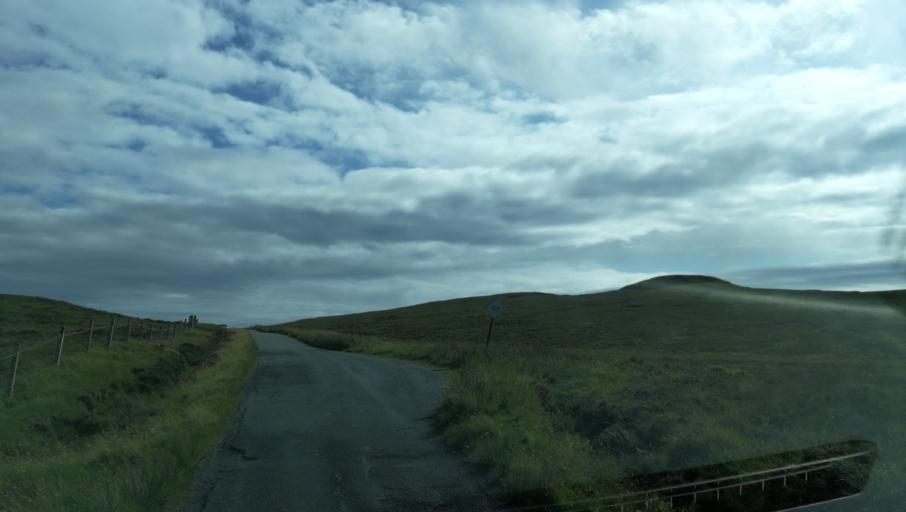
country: GB
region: Scotland
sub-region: Highland
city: Isle of Skye
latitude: 57.4133
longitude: -6.5666
